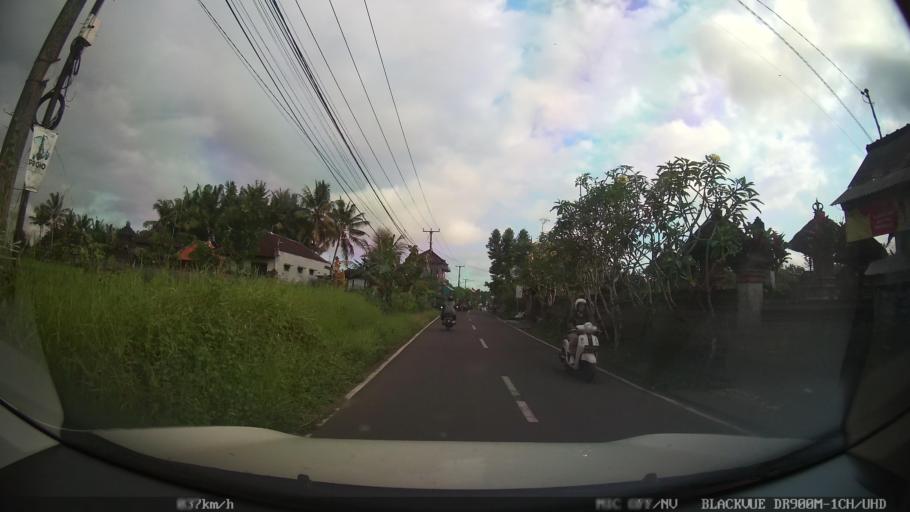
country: ID
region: Bali
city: Banjar Tebongkang
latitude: -8.5260
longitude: 115.2486
